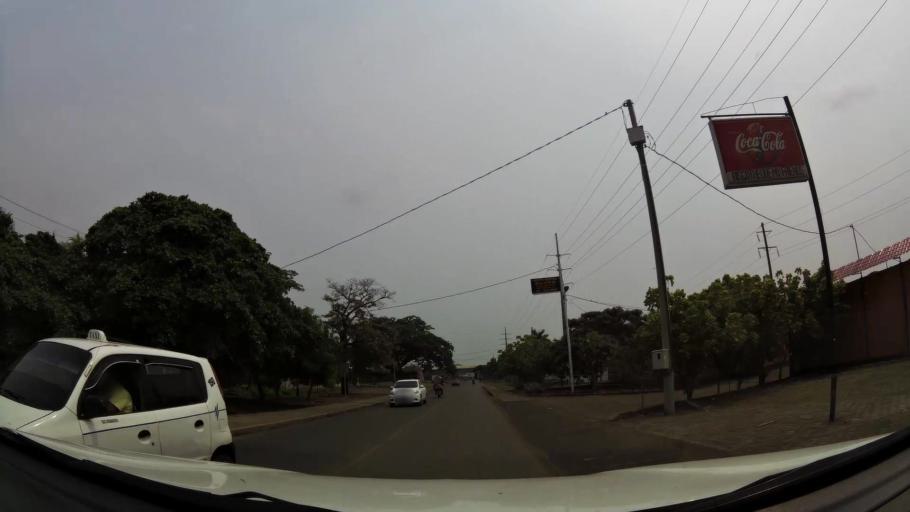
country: NI
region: Chinandega
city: Chinandega
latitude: 12.6455
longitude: -87.1281
